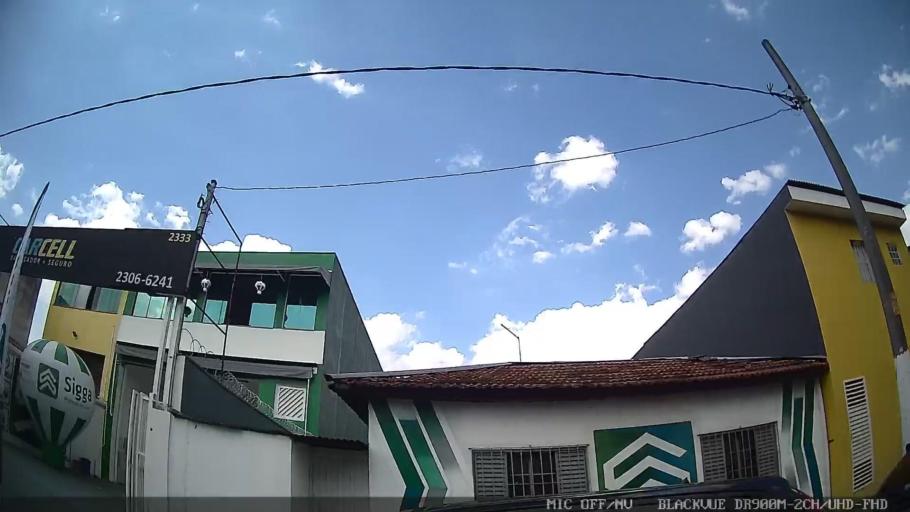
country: BR
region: Sao Paulo
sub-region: Guarulhos
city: Guarulhos
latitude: -23.5249
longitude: -46.4919
